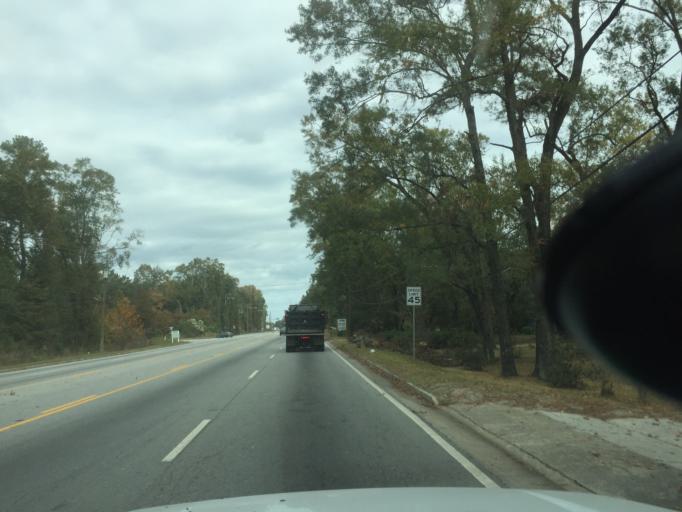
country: US
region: Georgia
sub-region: Chatham County
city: Garden City
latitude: 32.0988
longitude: -81.1961
